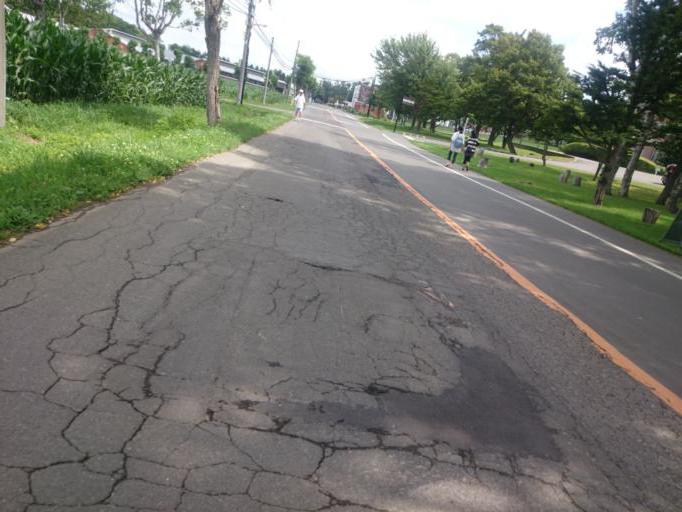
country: JP
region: Hokkaido
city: Ebetsu
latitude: 43.0741
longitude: 141.5087
